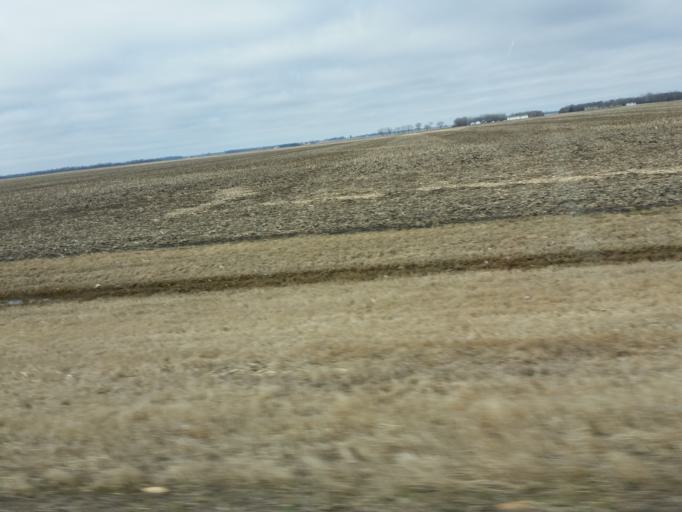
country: US
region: North Dakota
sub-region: Cass County
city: Casselton
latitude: 46.9761
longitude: -97.2188
